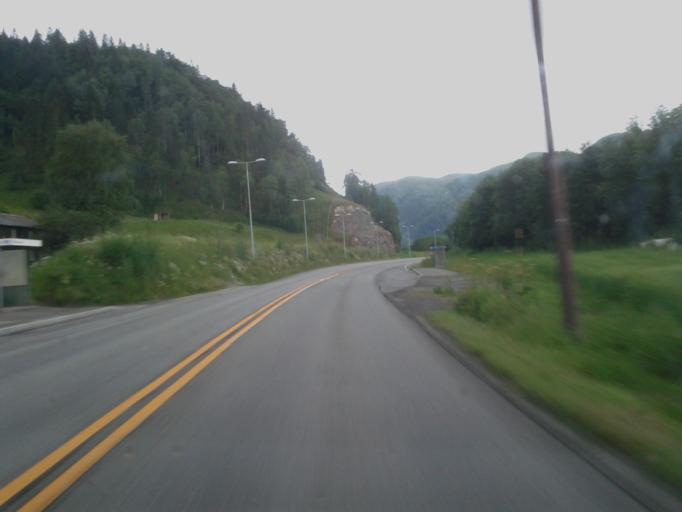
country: NO
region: Sor-Trondelag
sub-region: Midtre Gauldal
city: Storen
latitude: 63.0905
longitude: 10.2495
